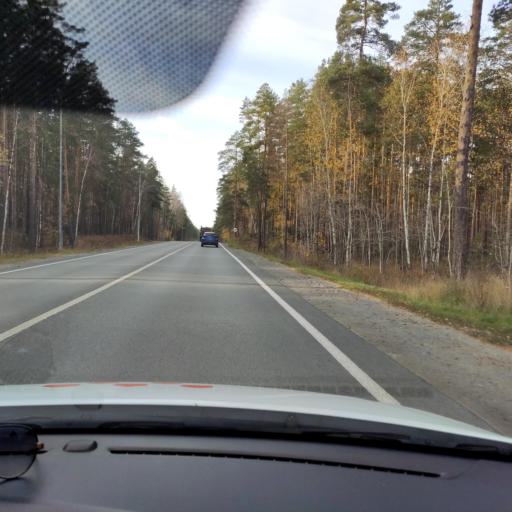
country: RU
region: Tatarstan
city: Verkhniy Uslon
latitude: 55.6382
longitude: 49.0443
